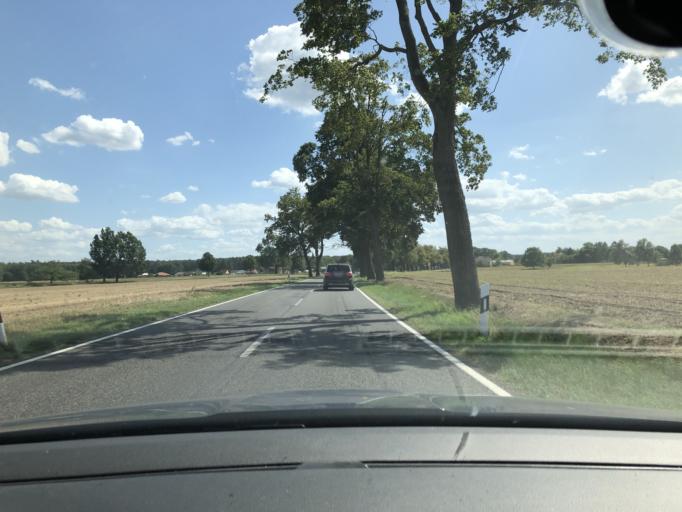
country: DE
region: Brandenburg
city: Ruthnick
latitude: 52.8859
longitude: 12.9965
